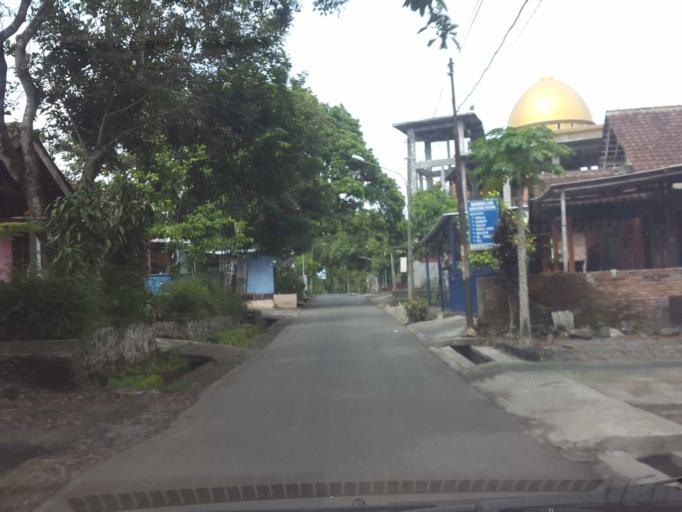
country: ID
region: Central Java
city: Salatiga
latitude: -7.3399
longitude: 110.5180
